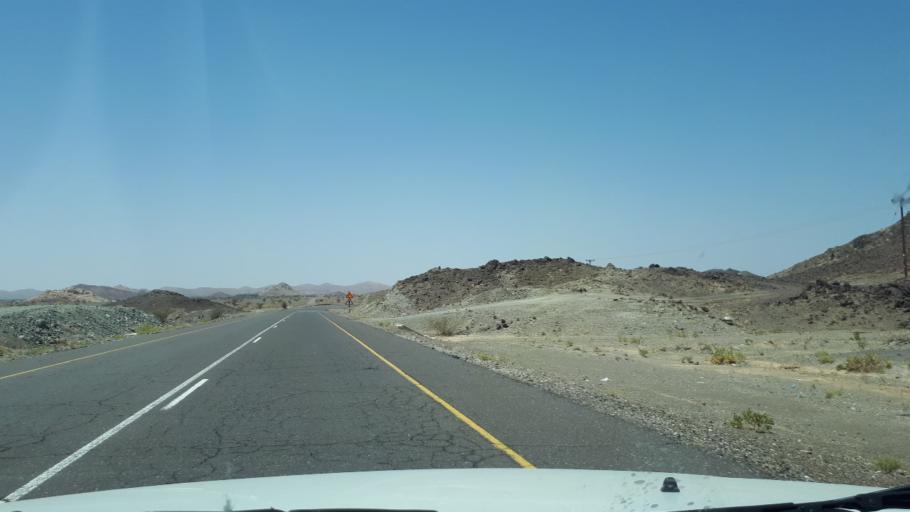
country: OM
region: Ash Sharqiyah
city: Ibra'
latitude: 22.6282
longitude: 58.4566
